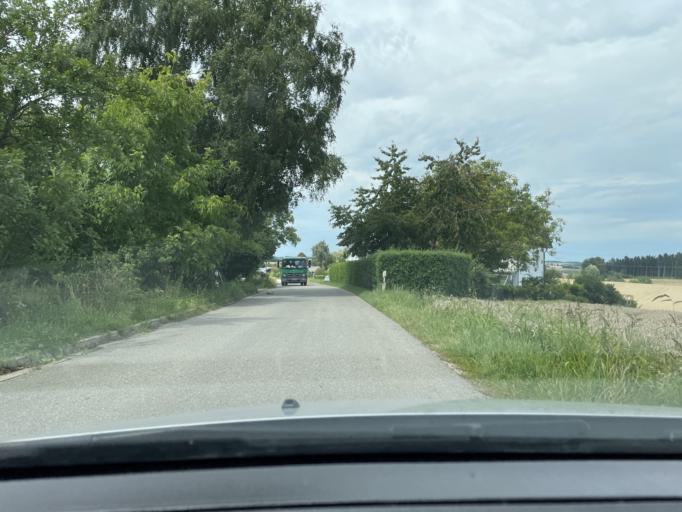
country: DE
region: Bavaria
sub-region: Lower Bavaria
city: Baierbach
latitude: 48.4451
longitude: 12.2245
